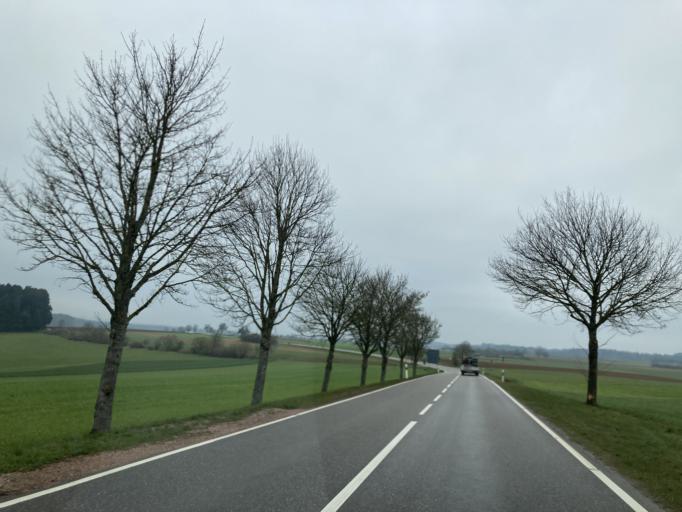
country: DE
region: Baden-Wuerttemberg
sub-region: Freiburg Region
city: Dornhan
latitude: 48.3428
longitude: 8.4729
